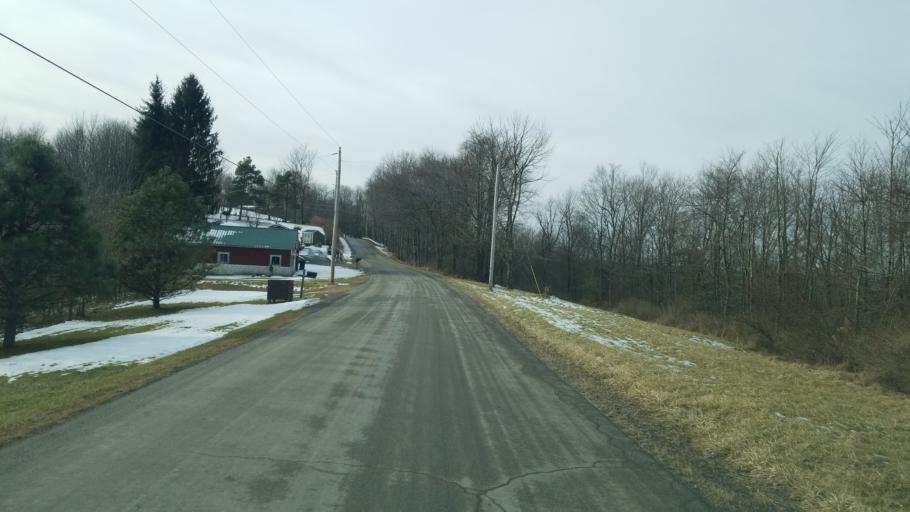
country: US
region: Pennsylvania
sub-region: Indiana County
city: Johnsonburg
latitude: 40.8369
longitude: -78.8868
